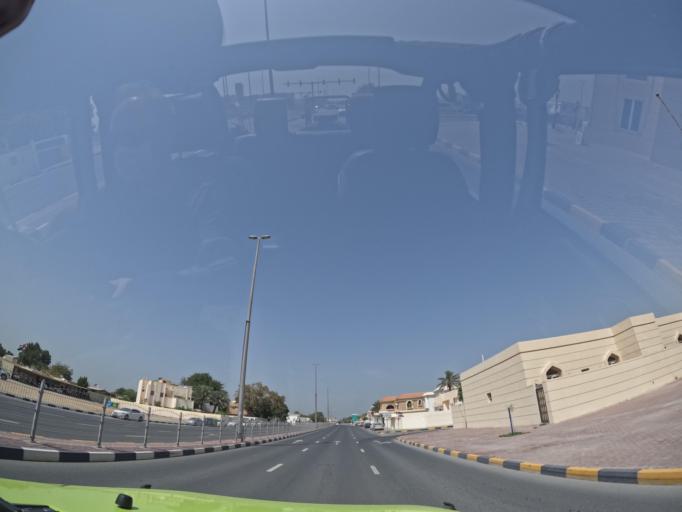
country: AE
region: Ajman
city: Ajman
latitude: 25.3774
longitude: 55.4225
